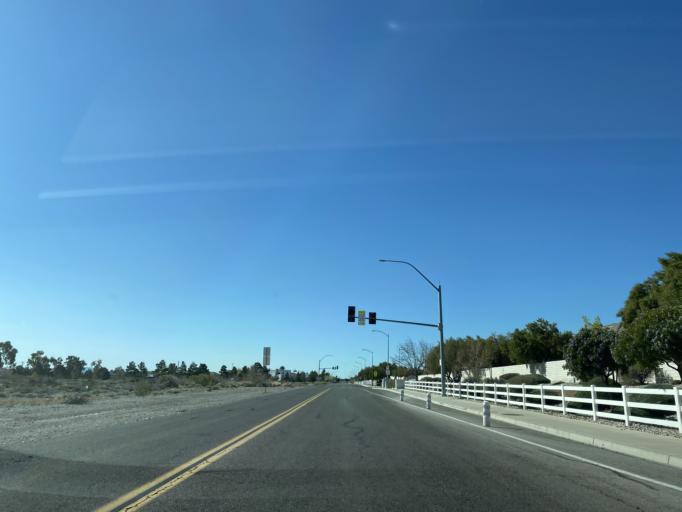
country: US
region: Nevada
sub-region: Clark County
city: Summerlin South
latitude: 36.3190
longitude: -115.2877
